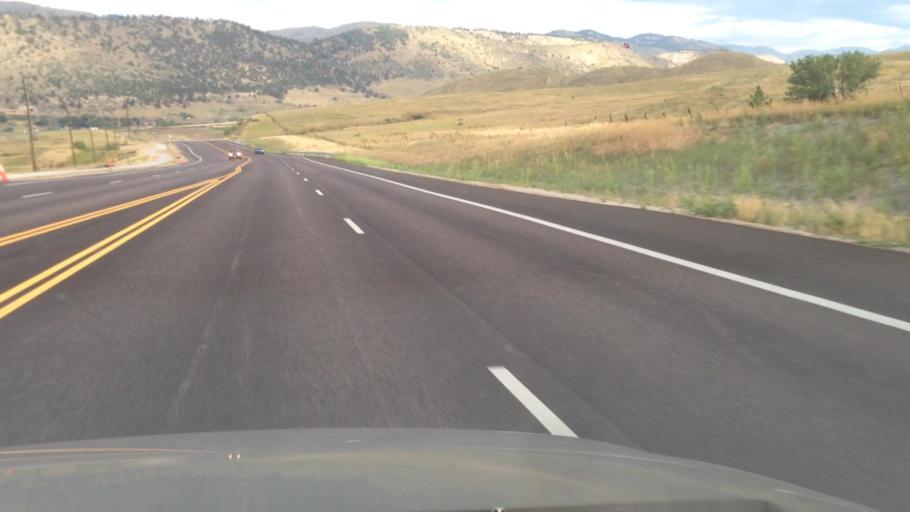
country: US
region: Colorado
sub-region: Jefferson County
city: West Pleasant View
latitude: 39.6820
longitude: -105.1743
